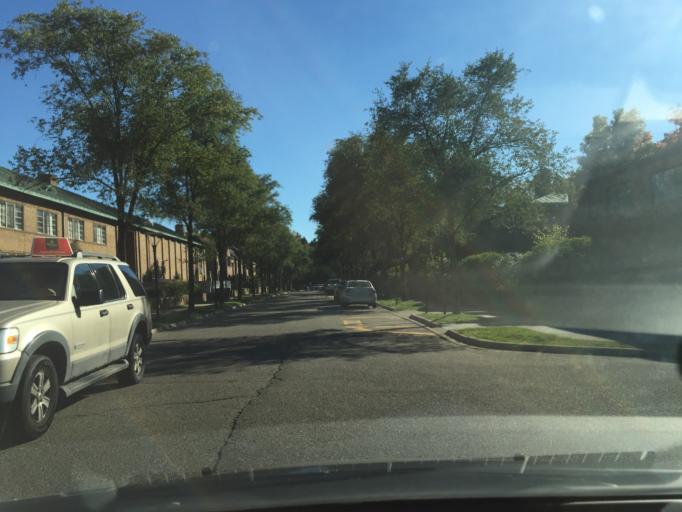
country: US
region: Michigan
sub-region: Oakland County
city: Bloomfield Hills
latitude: 42.5691
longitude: -83.2516
